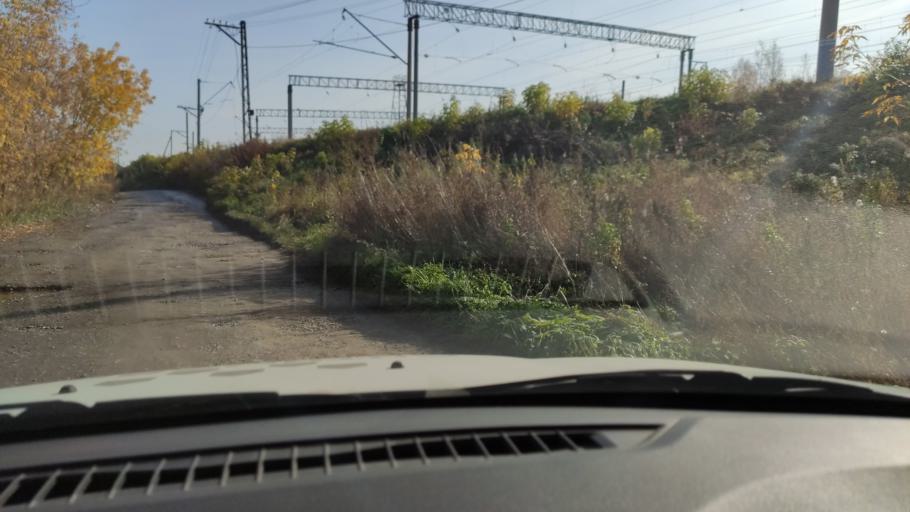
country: RU
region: Perm
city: Sylva
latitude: 58.0450
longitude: 56.7394
